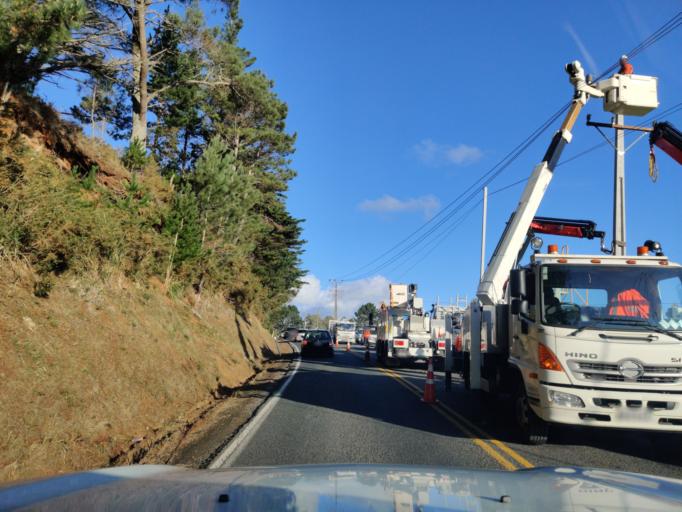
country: NZ
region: Auckland
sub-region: Auckland
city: Red Hill
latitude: -36.9696
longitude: 174.9853
